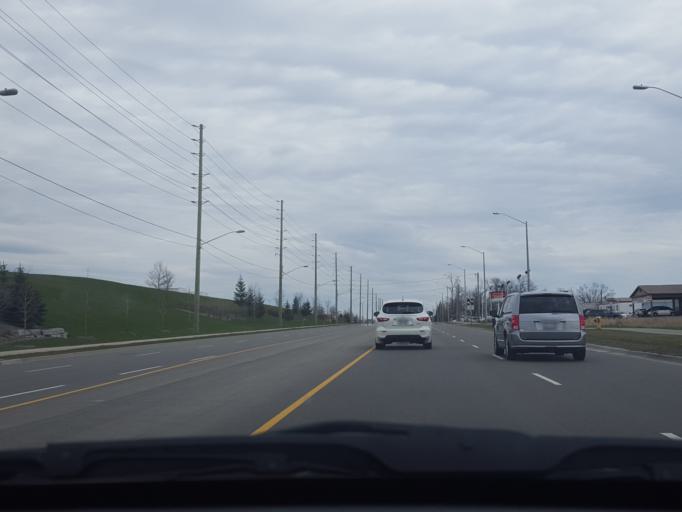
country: CA
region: Ontario
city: Ajax
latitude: 43.8488
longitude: -78.9964
